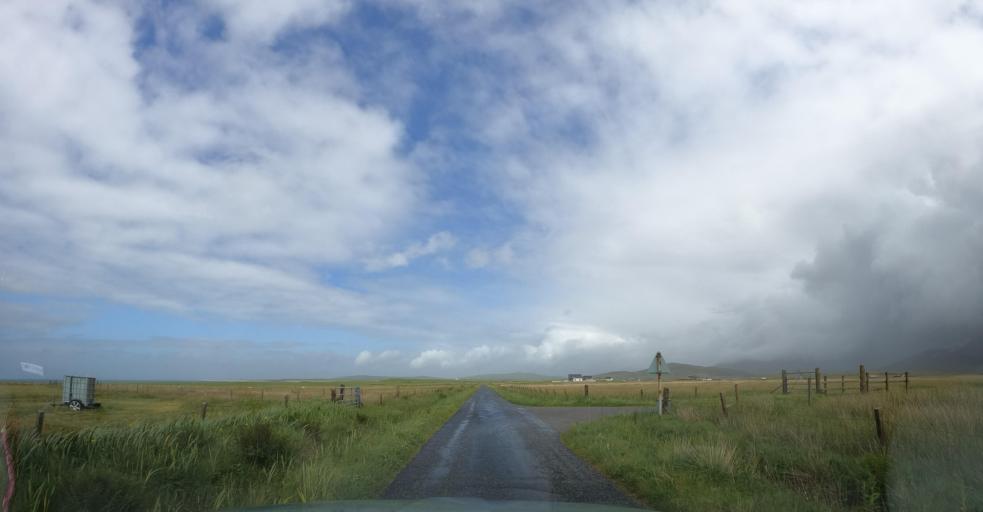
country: GB
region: Scotland
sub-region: Eilean Siar
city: Isle of South Uist
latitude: 57.2887
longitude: -7.4112
